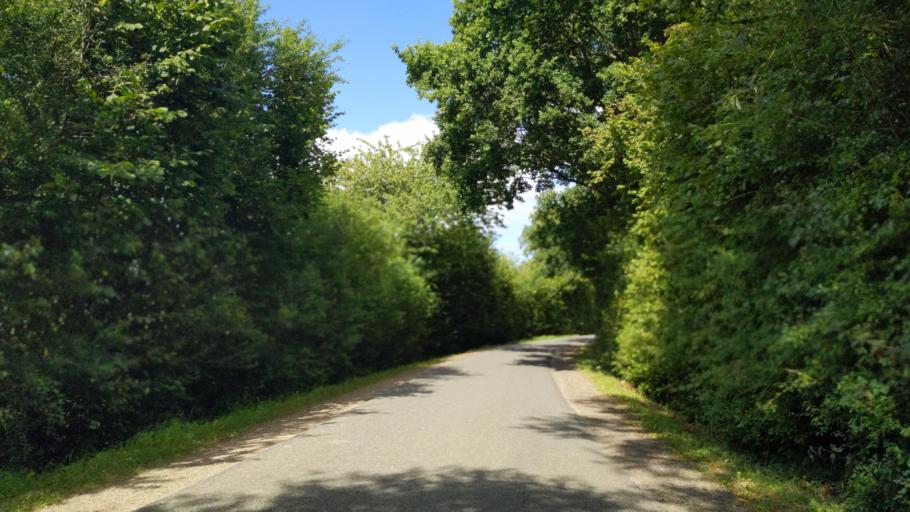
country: DE
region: Schleswig-Holstein
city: Monkhagen
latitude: 53.9088
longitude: 10.5928
